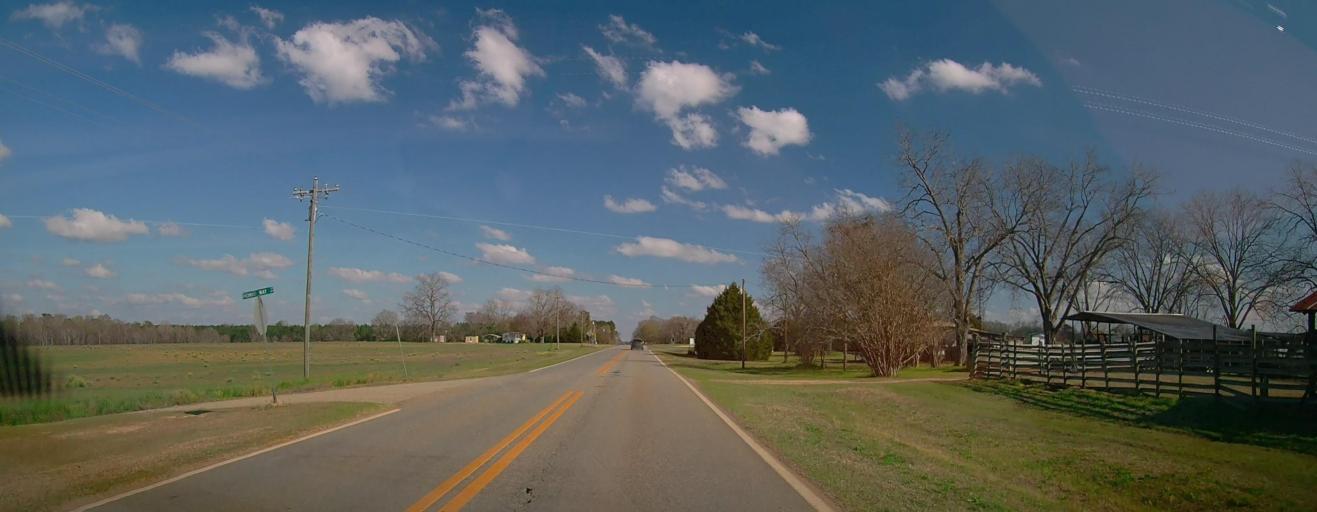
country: US
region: Georgia
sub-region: Laurens County
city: Dublin
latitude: 32.5651
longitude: -83.0232
